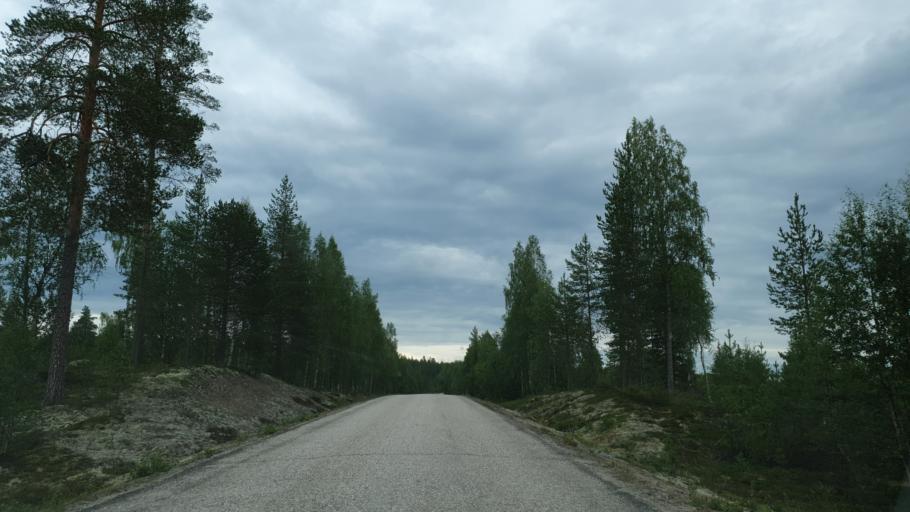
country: FI
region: Kainuu
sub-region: Kehys-Kainuu
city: Kuhmo
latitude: 64.3392
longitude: 29.3282
